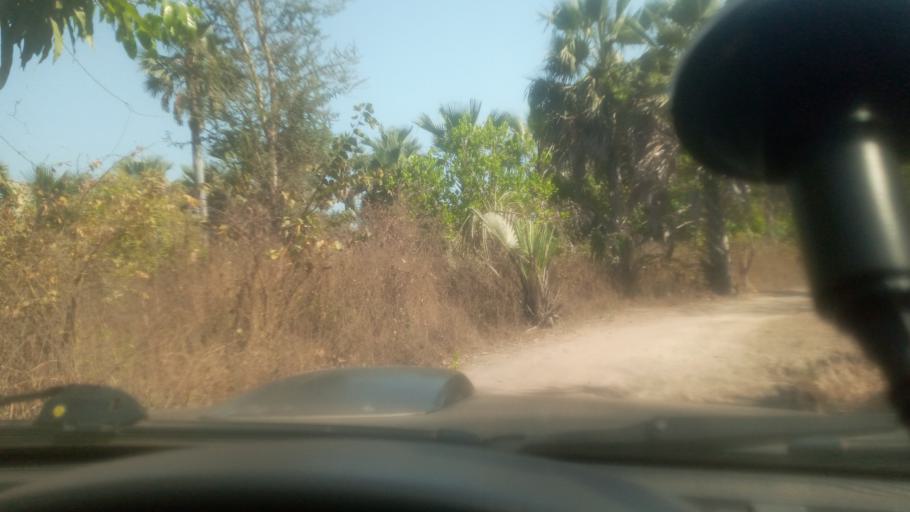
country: GW
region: Oio
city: Farim
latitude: 12.4566
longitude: -15.4087
